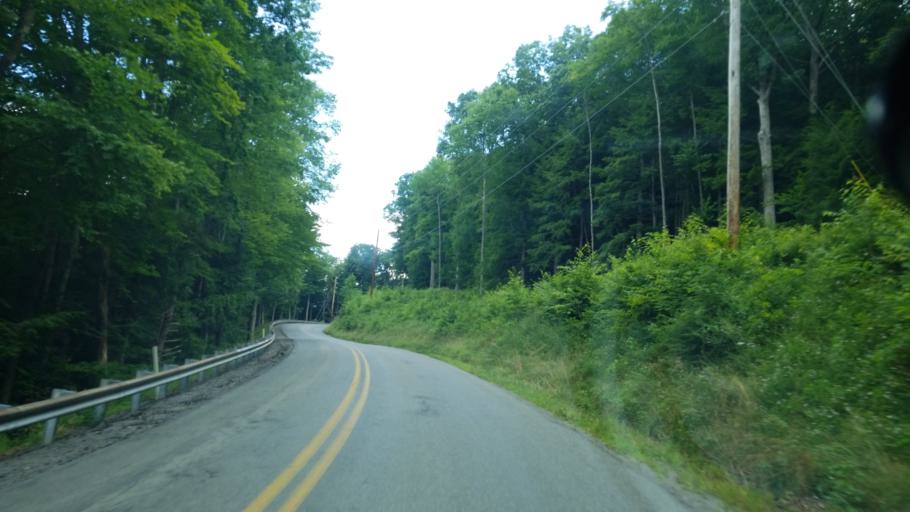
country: US
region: Pennsylvania
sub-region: Jefferson County
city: Brookville
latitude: 41.2353
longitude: -79.0470
